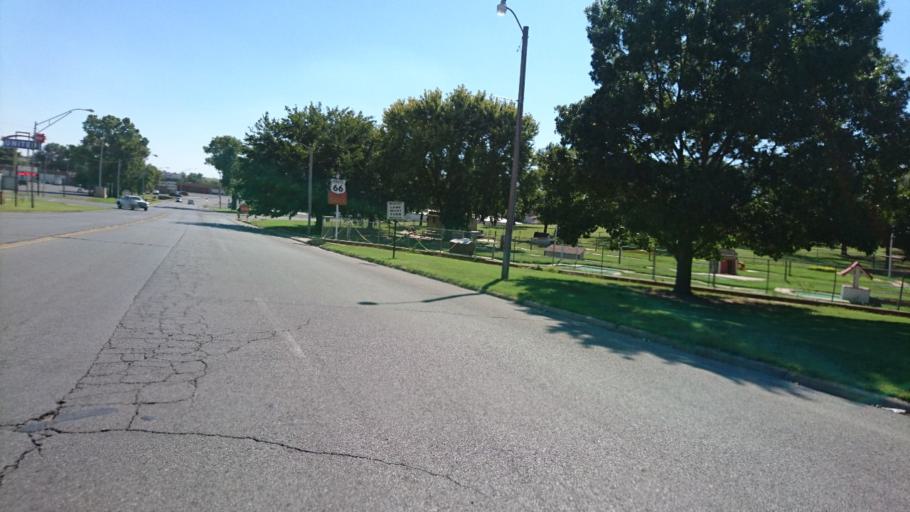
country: US
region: Oklahoma
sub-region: Custer County
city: Clinton
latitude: 35.5060
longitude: -98.9720
